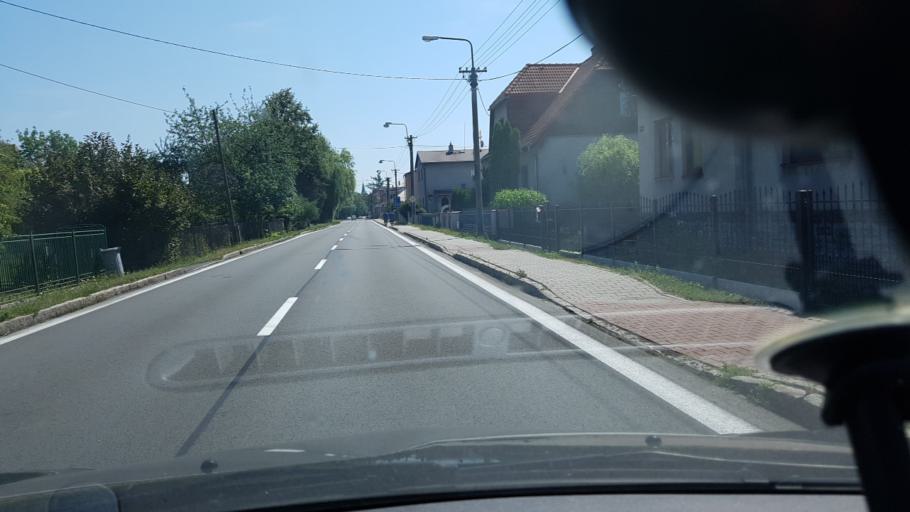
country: CZ
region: Moravskoslezsky
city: Stary Bohumin
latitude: 49.9065
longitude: 18.3443
